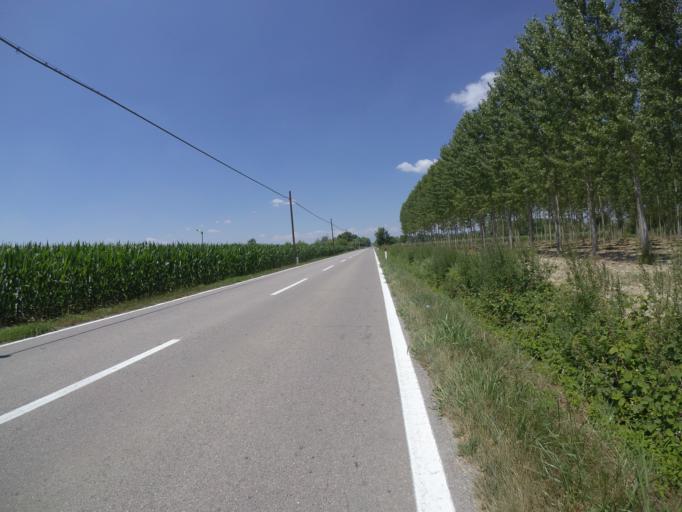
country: IT
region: Friuli Venezia Giulia
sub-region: Provincia di Udine
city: Rivignano
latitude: 45.8918
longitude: 13.0320
